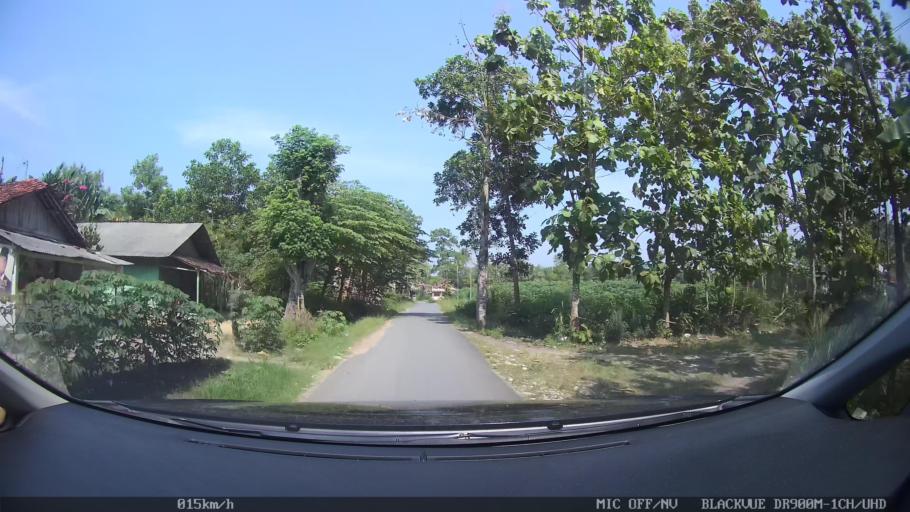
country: ID
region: Lampung
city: Natar
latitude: -5.2539
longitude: 105.1932
